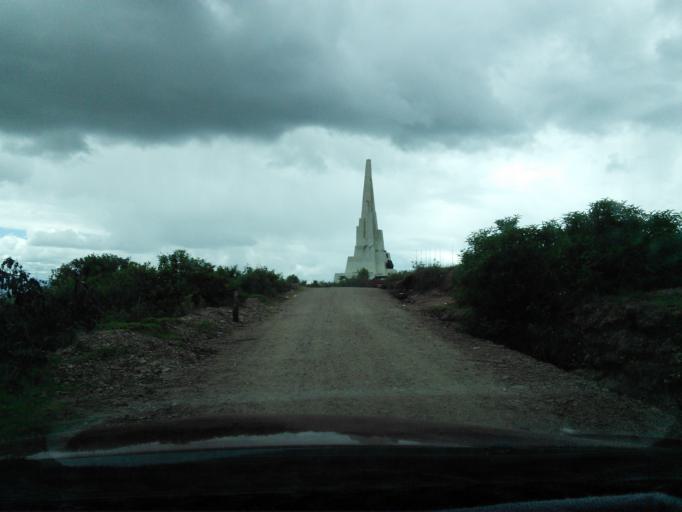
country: PE
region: Ayacucho
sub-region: Provincia de Huamanga
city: Quinua
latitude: -13.0430
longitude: -74.1299
